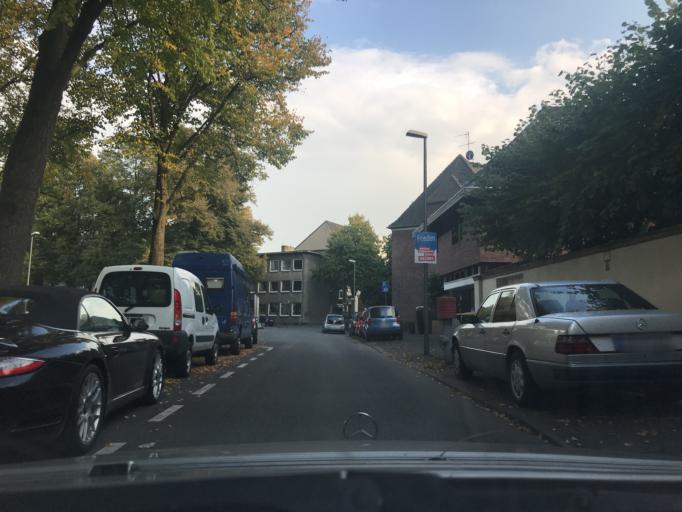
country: DE
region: North Rhine-Westphalia
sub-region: Regierungsbezirk Dusseldorf
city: Krefeld
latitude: 51.3386
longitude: 6.5779
